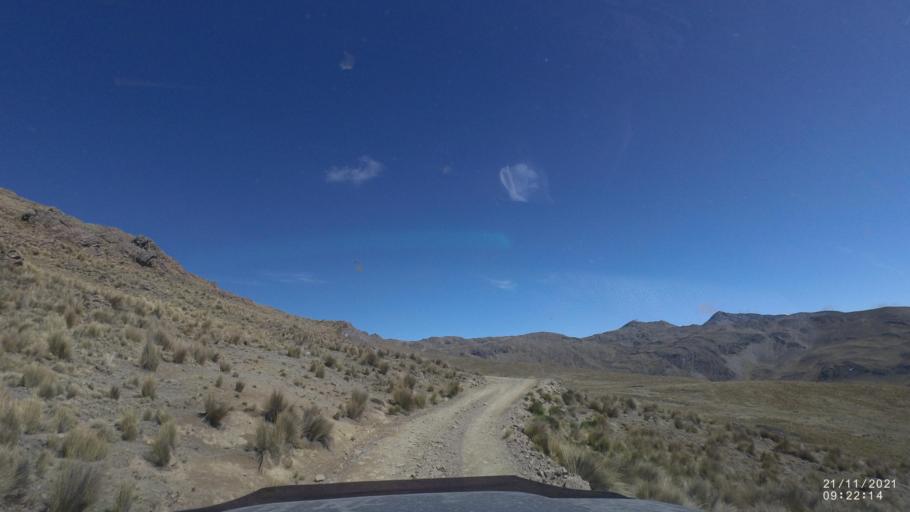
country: BO
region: Cochabamba
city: Cochabamba
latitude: -17.1019
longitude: -66.2481
